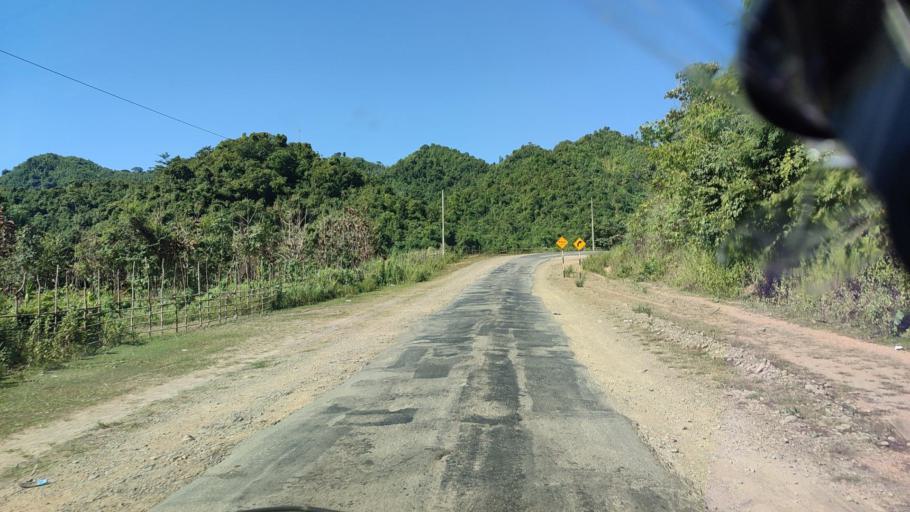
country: MM
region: Rakhine
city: Sittwe
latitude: 19.9757
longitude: 93.6462
